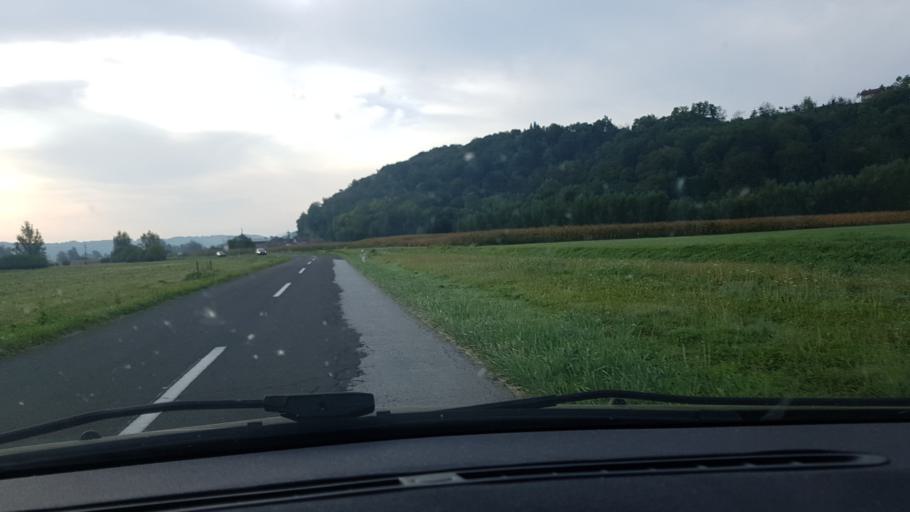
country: HR
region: Krapinsko-Zagorska
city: Mihovljan
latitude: 46.1048
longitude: 16.0179
